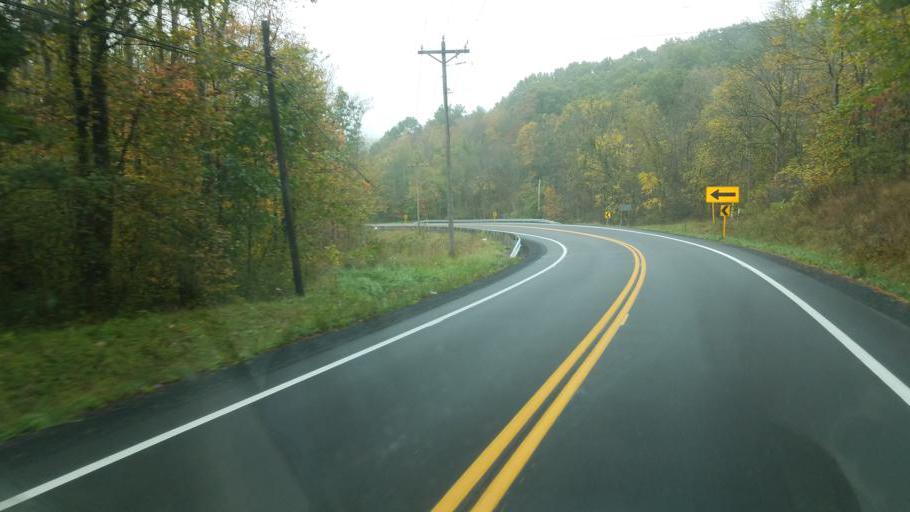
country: US
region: Ohio
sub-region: Carroll County
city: Carrollton
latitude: 40.5072
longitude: -81.1127
